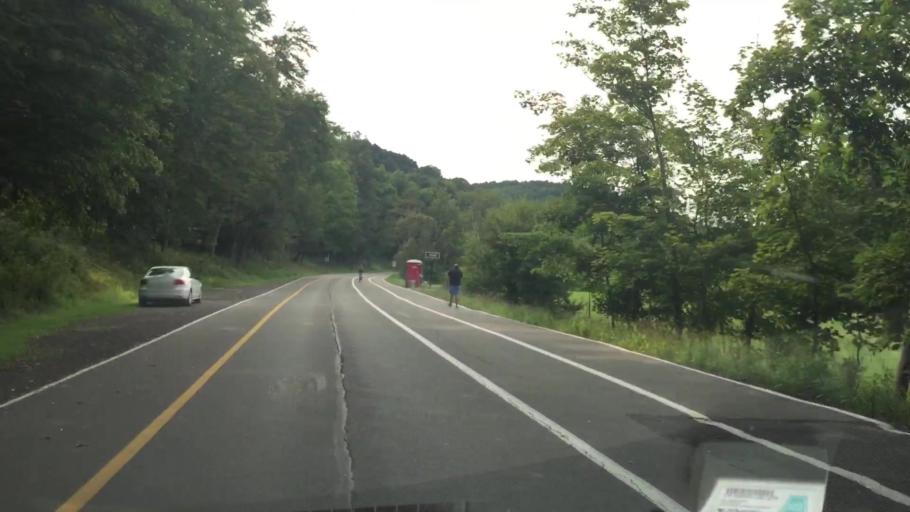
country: US
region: Pennsylvania
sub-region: Allegheny County
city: Gibsonia
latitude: 40.6045
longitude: -80.0112
